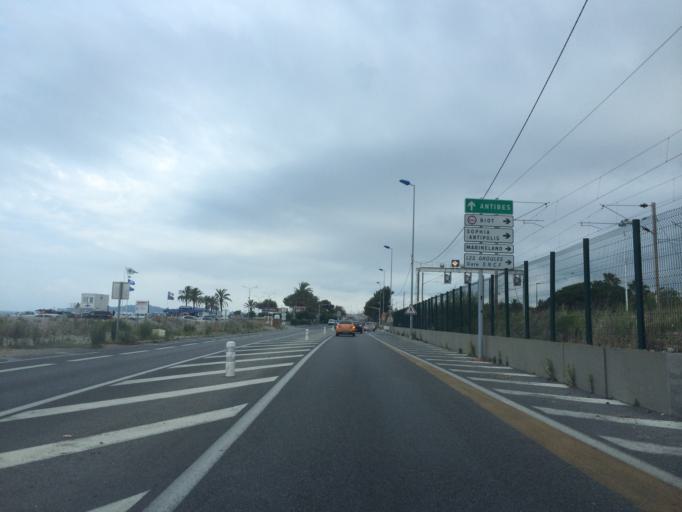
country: FR
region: Provence-Alpes-Cote d'Azur
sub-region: Departement des Alpes-Maritimes
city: Biot
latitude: 43.6130
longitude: 7.1274
